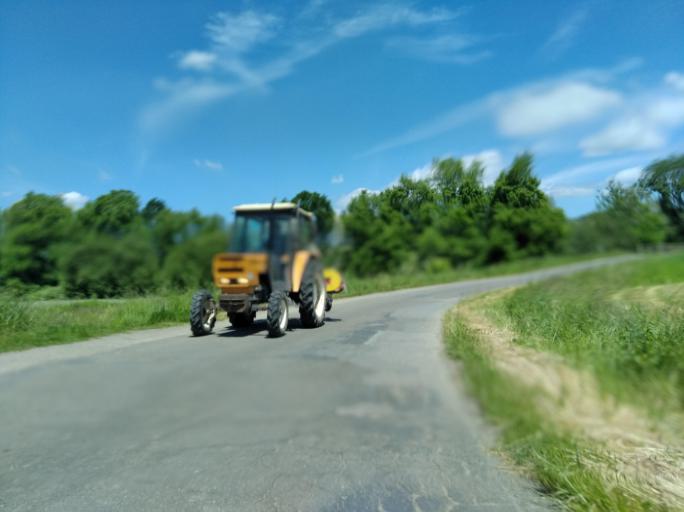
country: PL
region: Subcarpathian Voivodeship
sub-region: Powiat krosnienski
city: Wojaszowka
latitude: 49.7843
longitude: 21.6801
